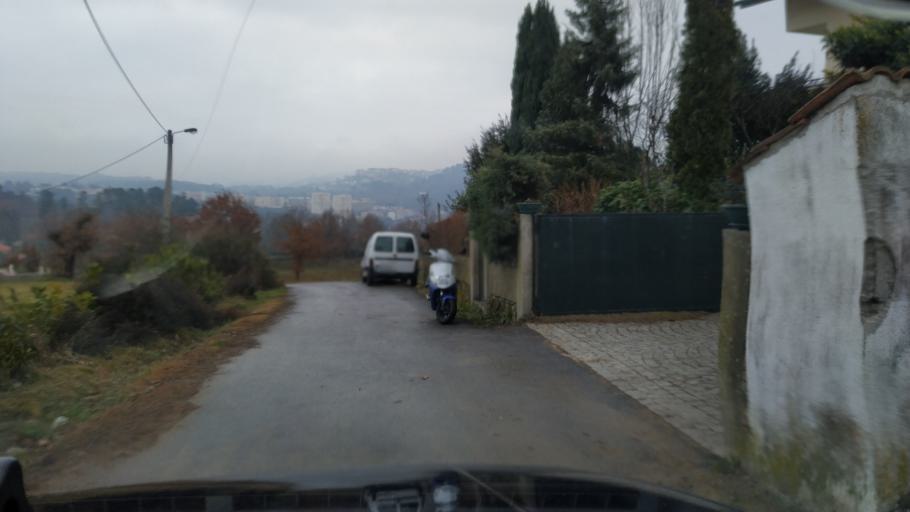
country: PT
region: Vila Real
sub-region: Vila Real
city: Vila Real
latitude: 41.2987
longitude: -7.7668
